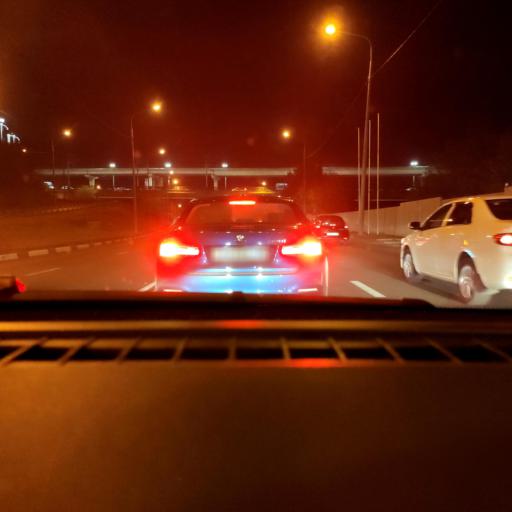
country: RU
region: Voronezj
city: Voronezh
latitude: 51.6920
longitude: 39.2330
